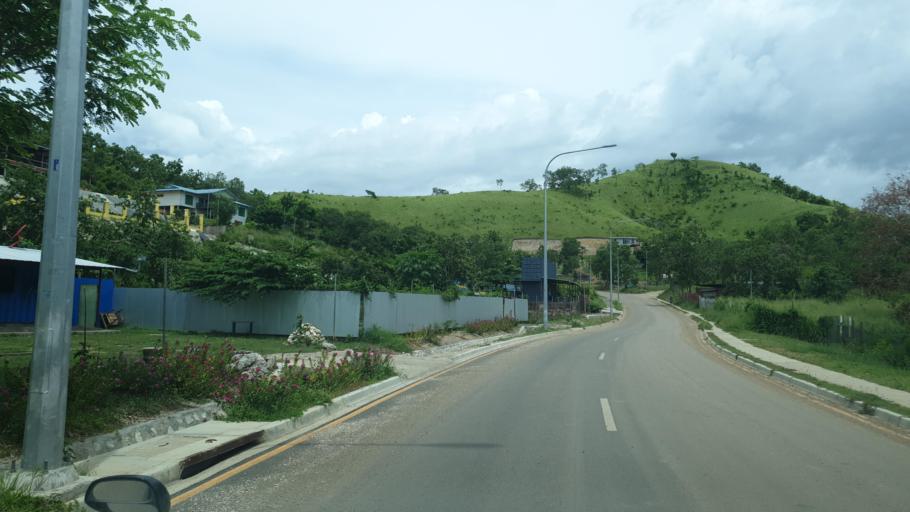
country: PG
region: National Capital
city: Port Moresby
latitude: -9.5274
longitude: 147.2482
